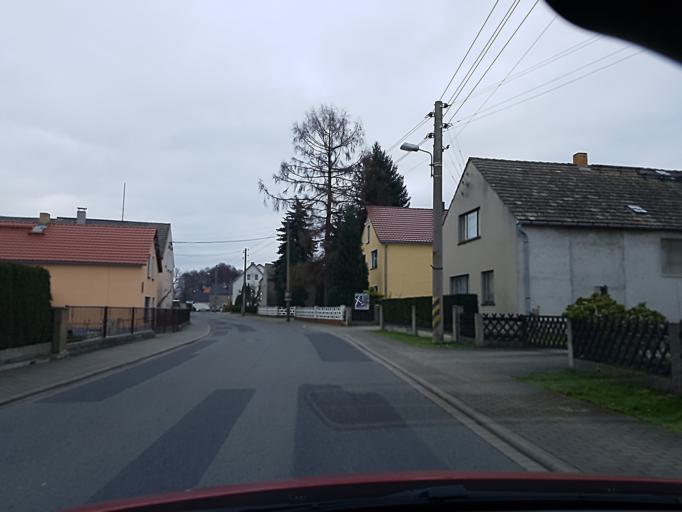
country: DE
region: Brandenburg
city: Merzdorf
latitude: 51.4041
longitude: 13.5430
